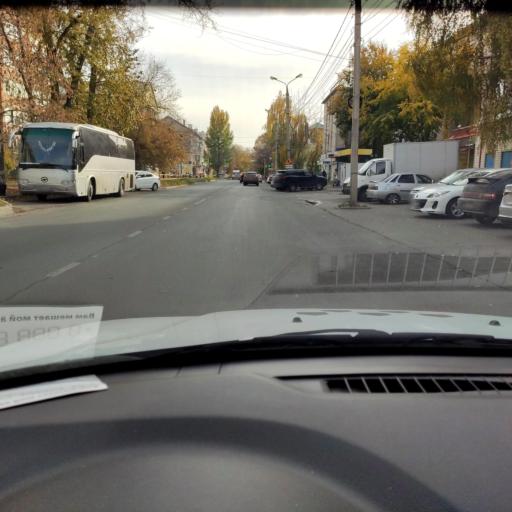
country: RU
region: Samara
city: Tol'yatti
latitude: 53.5084
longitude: 49.4070
